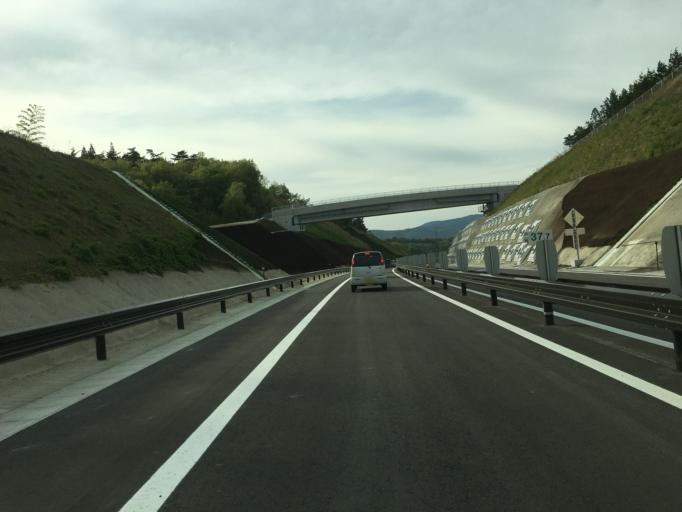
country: JP
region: Fukushima
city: Hobaramachi
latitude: 37.7923
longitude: 140.5515
